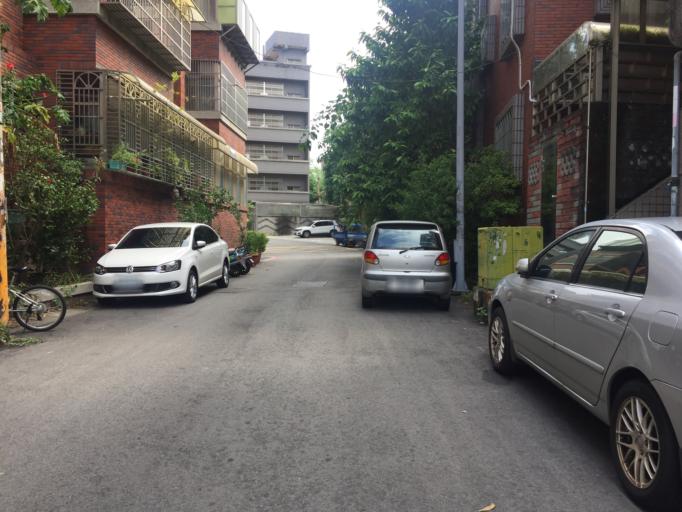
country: TW
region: Taiwan
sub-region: Hsinchu
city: Hsinchu
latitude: 24.7956
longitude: 120.9787
